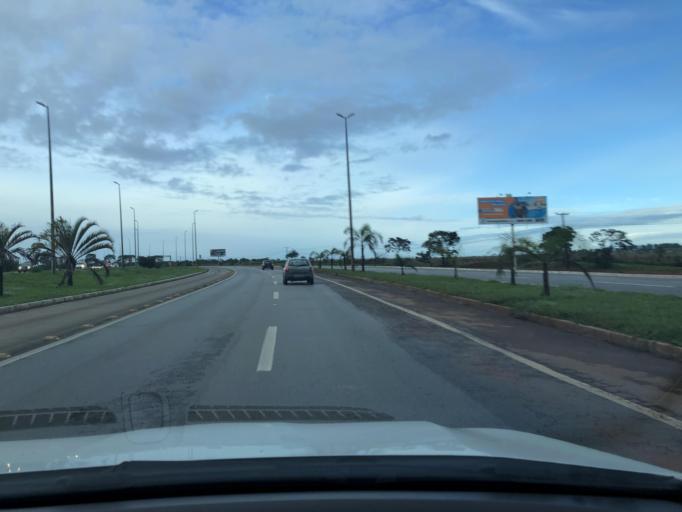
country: BR
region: Federal District
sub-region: Brasilia
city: Brasilia
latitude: -15.9492
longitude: -47.9934
